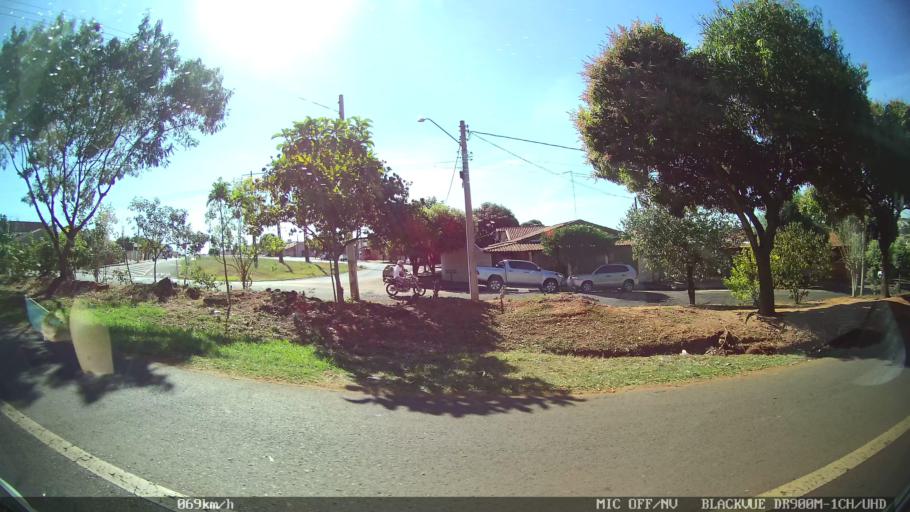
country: BR
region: Sao Paulo
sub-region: Olimpia
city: Olimpia
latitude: -20.7380
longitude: -48.8874
